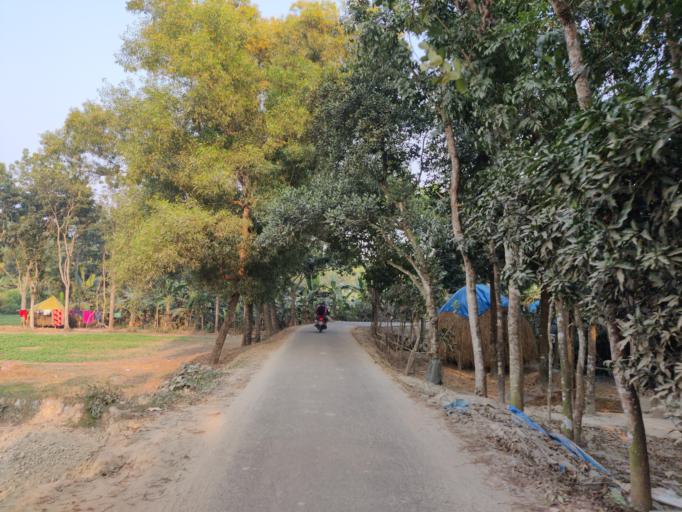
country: BD
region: Dhaka
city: Narsingdi
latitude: 24.0950
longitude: 90.7156
